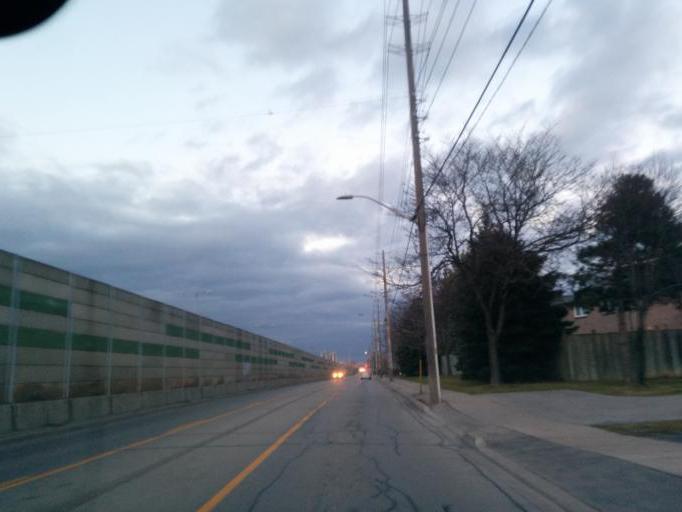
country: CA
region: Ontario
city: Etobicoke
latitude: 43.5865
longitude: -79.5795
